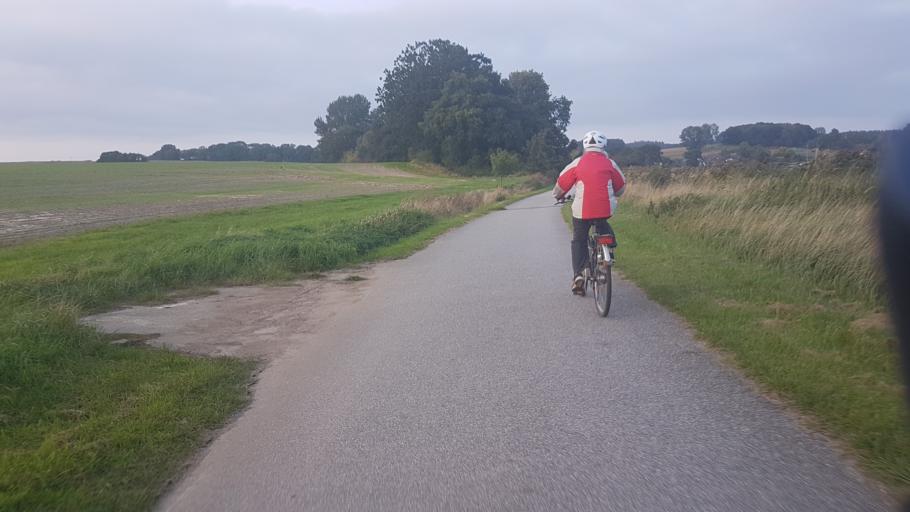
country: DE
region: Mecklenburg-Vorpommern
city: Ostseebad Binz
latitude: 54.3491
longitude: 13.5683
